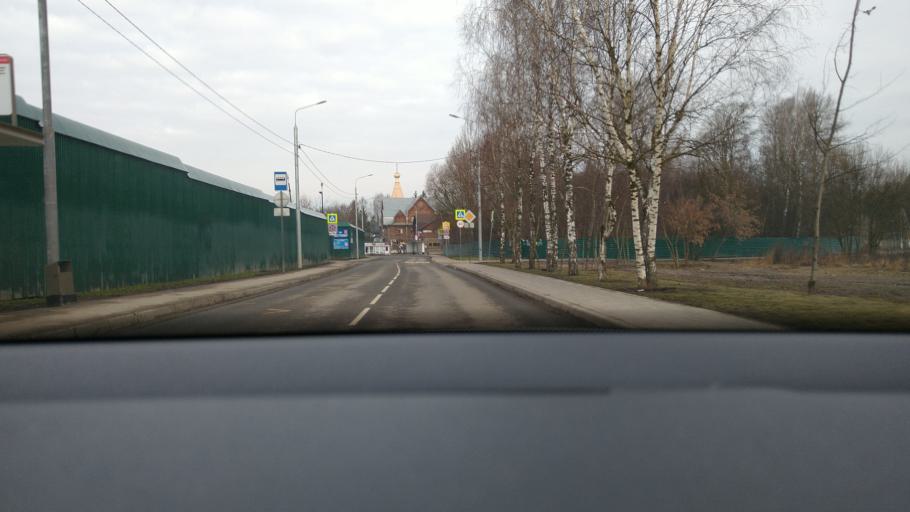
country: RU
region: Moskovskaya
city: Vatutinki
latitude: 55.5157
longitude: 37.3379
